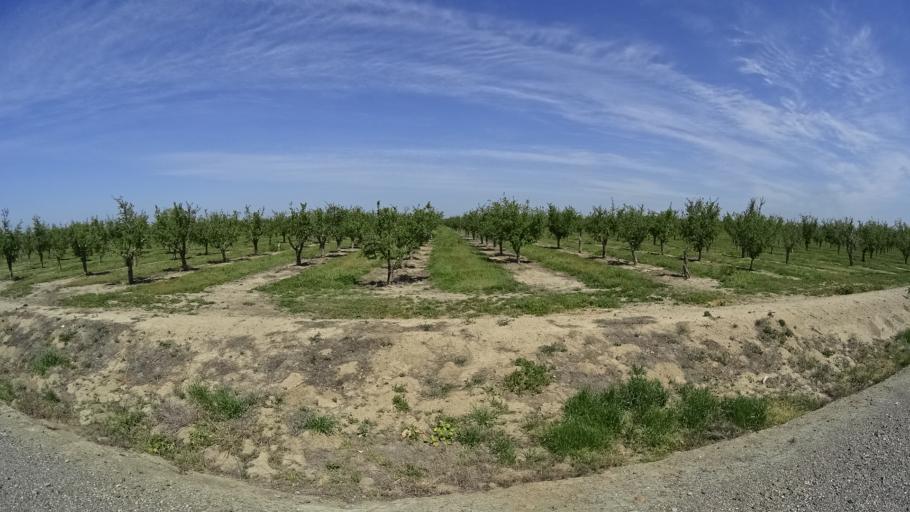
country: US
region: California
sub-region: Glenn County
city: Orland
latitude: 39.6528
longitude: -122.1284
